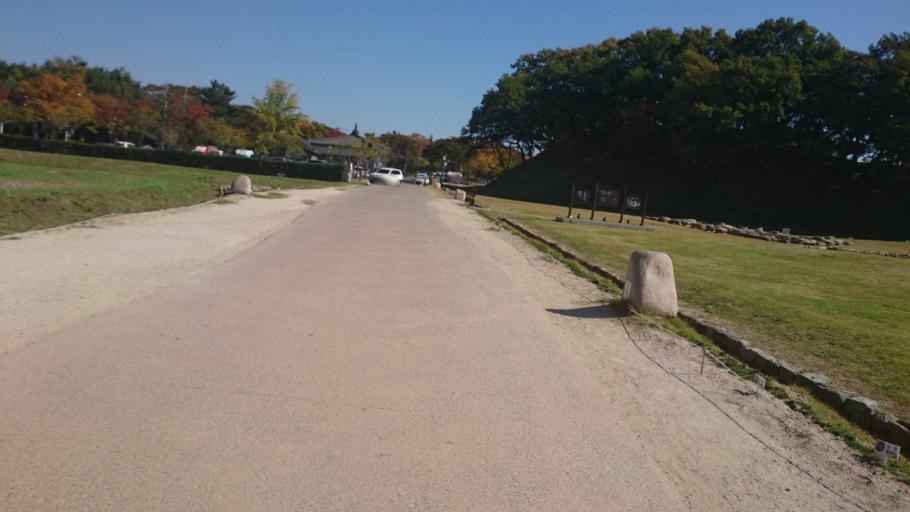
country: KR
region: Gyeongsangbuk-do
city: Kyonju
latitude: 35.8339
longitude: 129.2233
